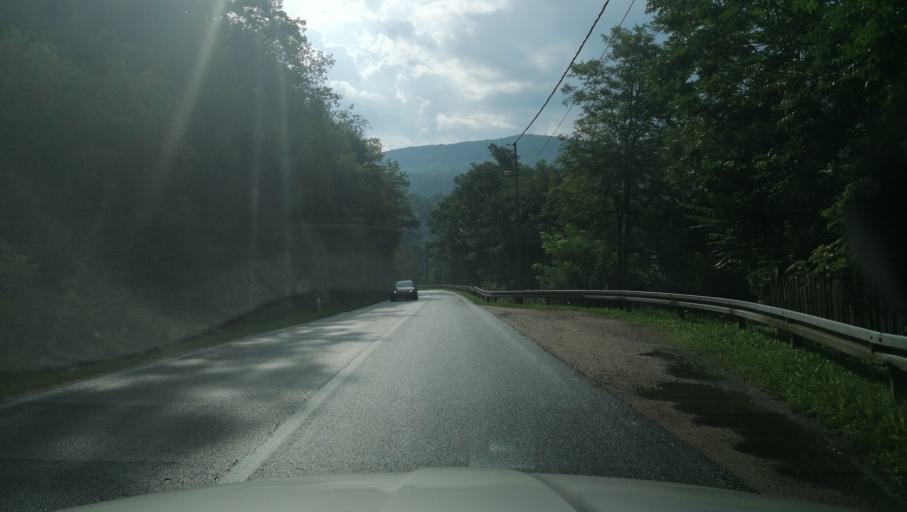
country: BA
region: Republika Srpska
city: Hiseti
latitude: 44.6754
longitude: 17.1504
